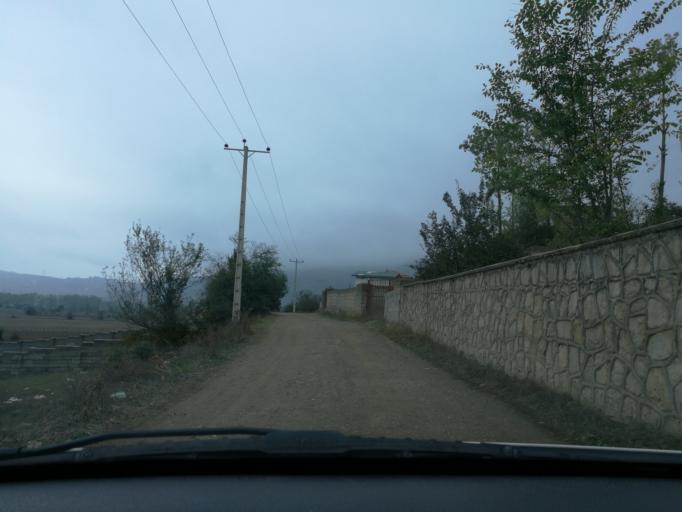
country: IR
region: Mazandaran
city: `Abbasabad
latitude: 36.5033
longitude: 51.2038
